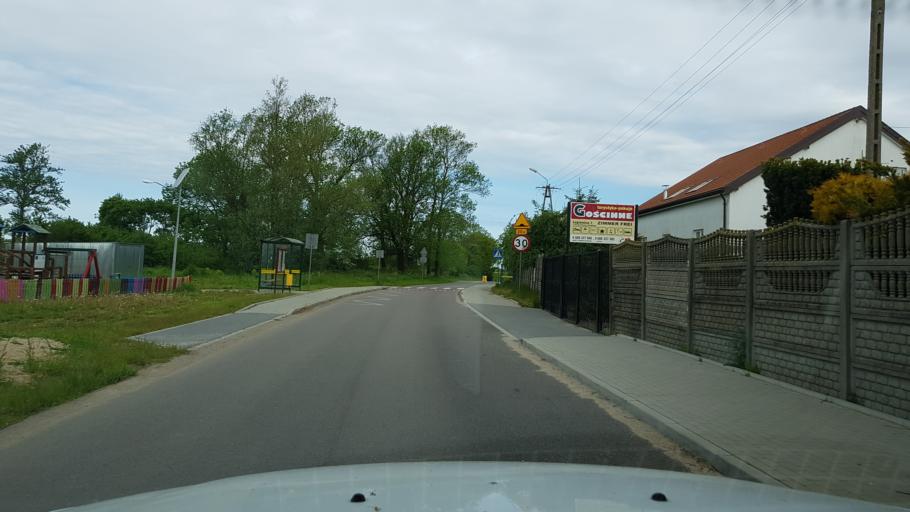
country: PL
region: West Pomeranian Voivodeship
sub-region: Powiat kolobrzeski
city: Ustronie Morskie
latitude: 54.2105
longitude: 15.8246
